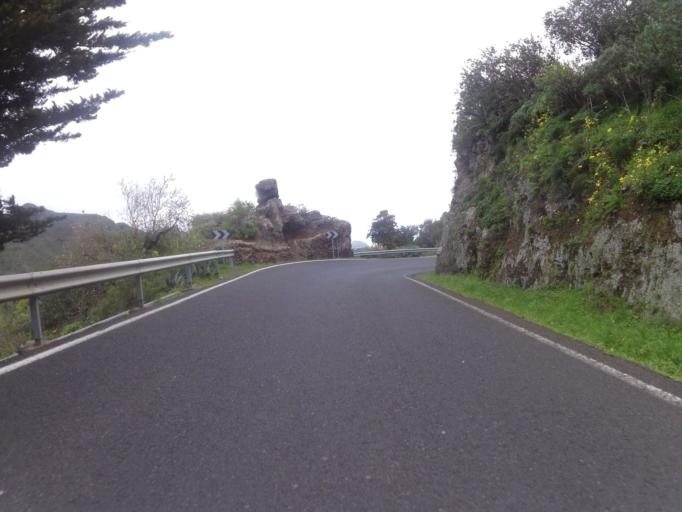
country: ES
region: Canary Islands
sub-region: Provincia de Las Palmas
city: Vega de San Mateo
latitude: 27.9945
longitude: -15.5247
